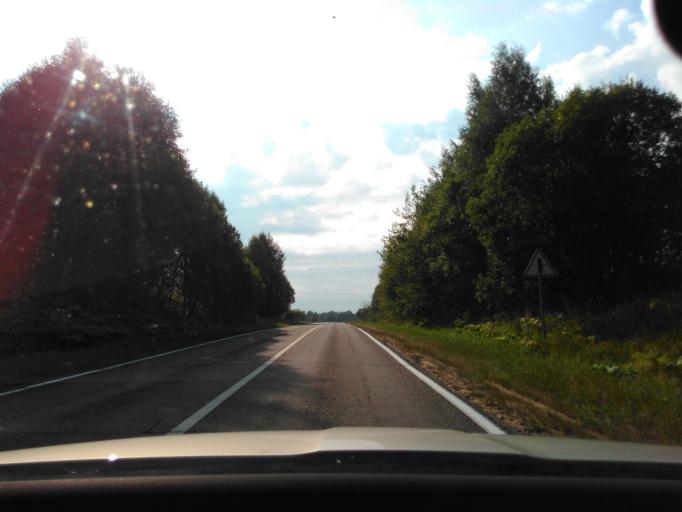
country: RU
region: Moskovskaya
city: Klin
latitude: 56.1941
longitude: 36.7259
